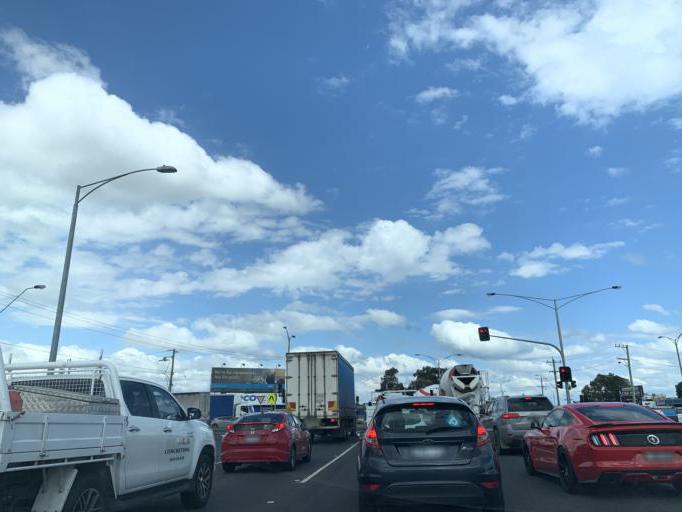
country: AU
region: Victoria
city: Heatherton
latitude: -37.9861
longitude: 145.1095
